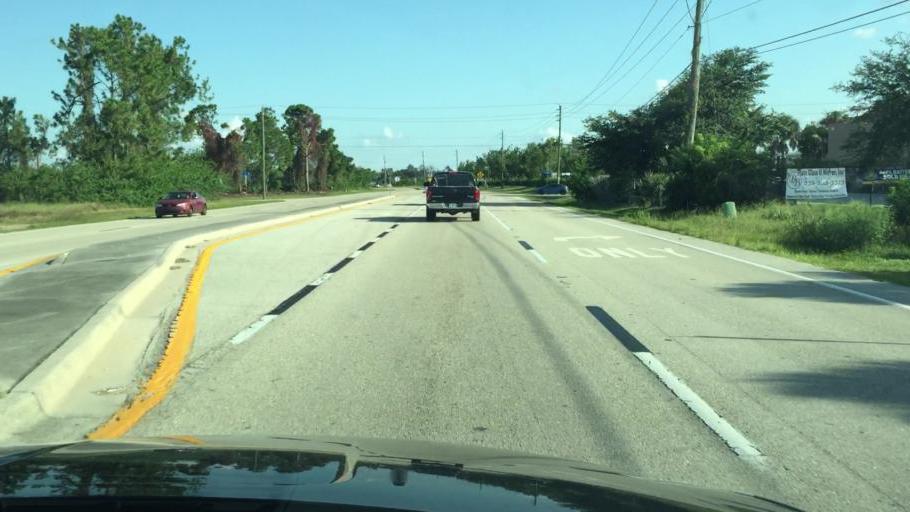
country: US
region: Florida
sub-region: Lee County
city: Gateway
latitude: 26.6165
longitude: -81.7488
